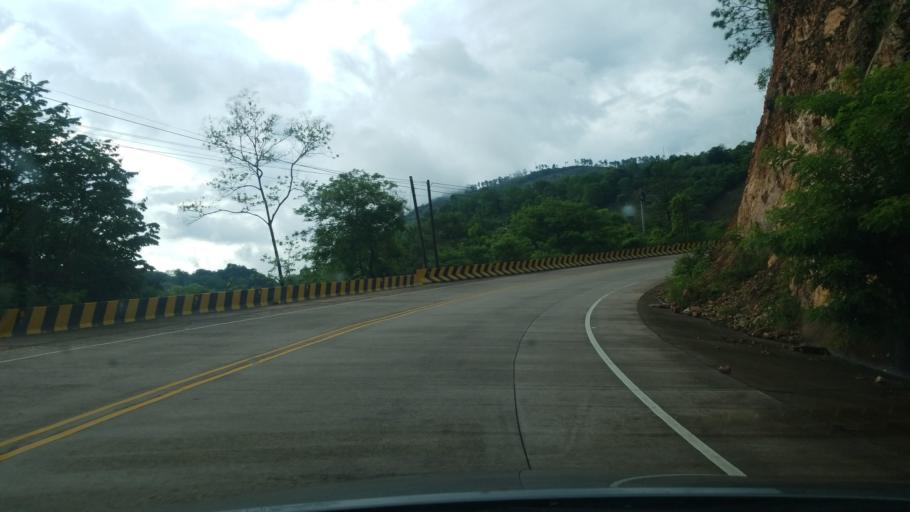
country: HN
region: Copan
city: Copan
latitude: 14.8388
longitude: -89.1866
